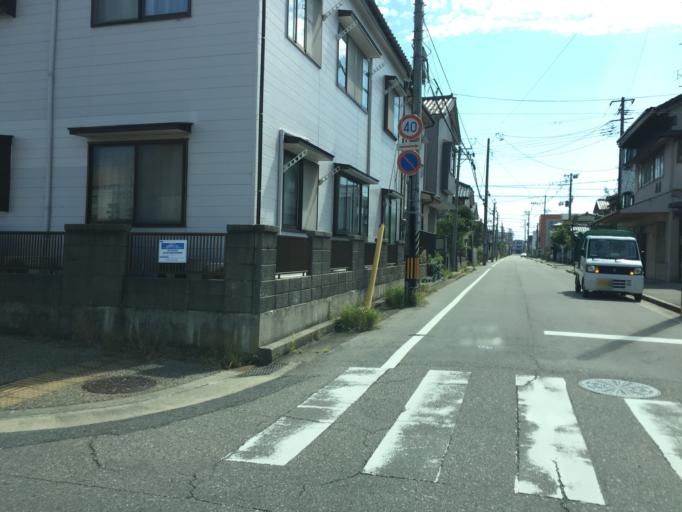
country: JP
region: Niigata
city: Niigata-shi
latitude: 37.9135
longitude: 139.0225
